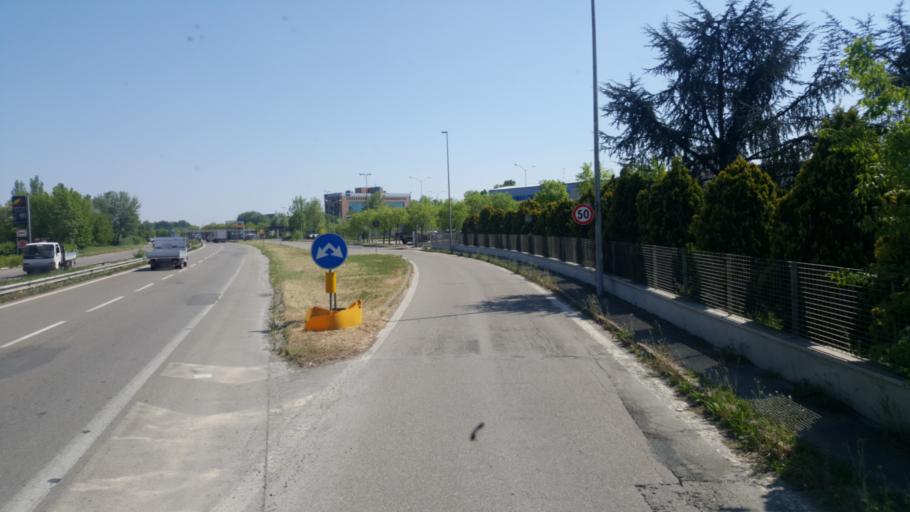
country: IT
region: Emilia-Romagna
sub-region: Provincia di Modena
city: Modena
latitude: 44.6543
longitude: 10.9564
